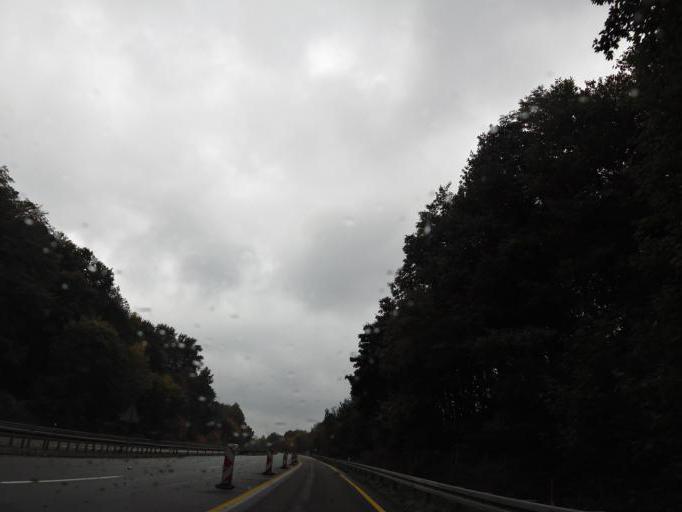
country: FR
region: Lorraine
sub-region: Departement de la Moselle
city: Alsting
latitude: 49.2102
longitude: 7.0173
